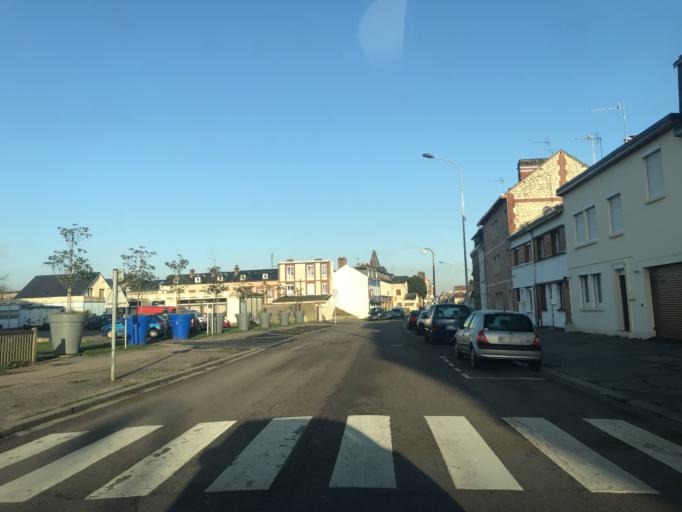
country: FR
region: Haute-Normandie
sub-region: Departement de la Seine-Maritime
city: Sotteville-les-Rouen
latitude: 49.4195
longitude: 1.0948
